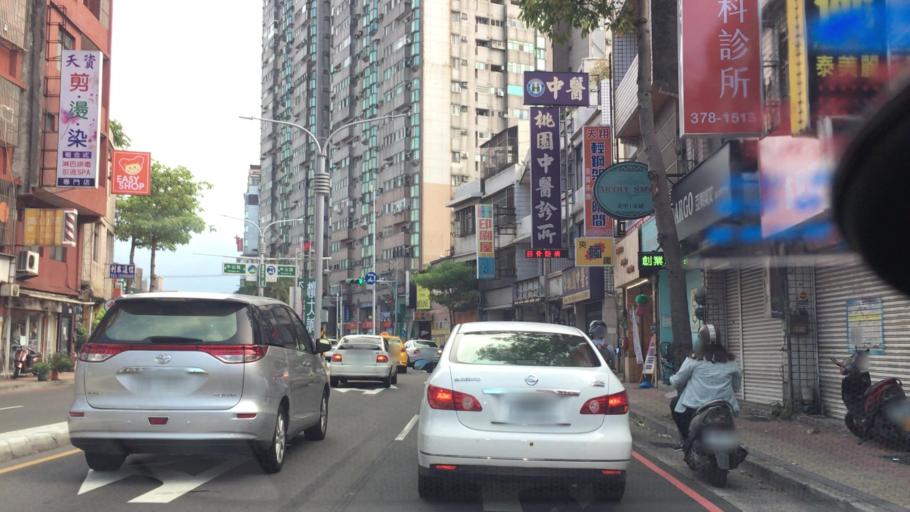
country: TW
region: Taiwan
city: Taoyuan City
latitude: 24.9906
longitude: 121.2884
